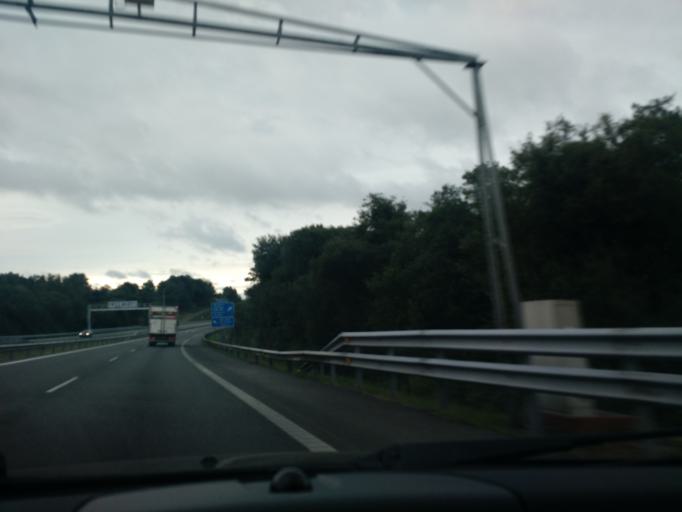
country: ES
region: Galicia
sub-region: Provincia da Coruna
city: Oleiros
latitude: 43.2939
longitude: -8.2998
